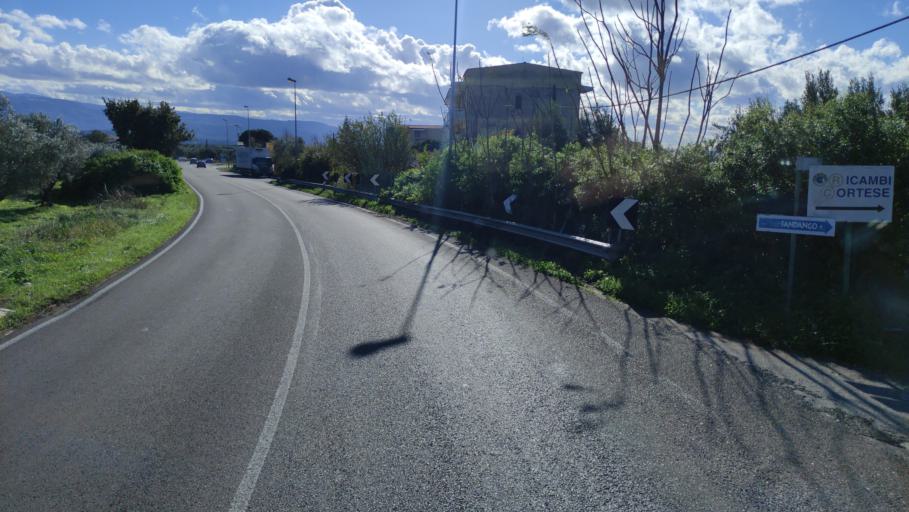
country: IT
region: Calabria
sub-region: Provincia di Catanzaro
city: Santa Eufemia Lamezia
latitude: 38.9302
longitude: 16.2855
